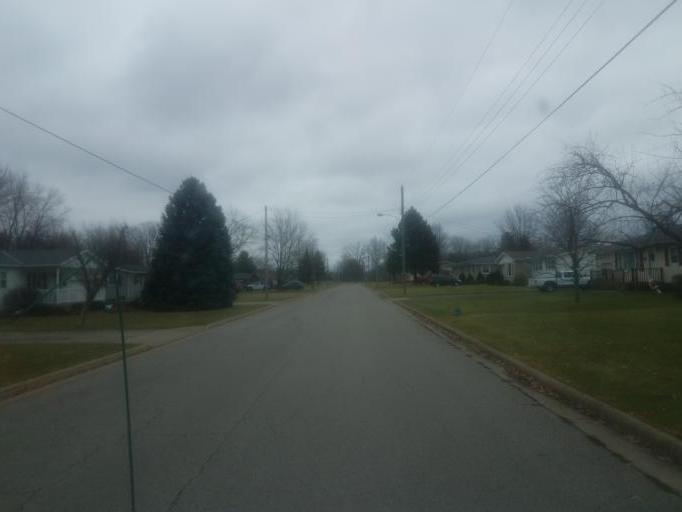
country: US
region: Ohio
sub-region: Crawford County
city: Crestline
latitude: 40.7743
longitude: -82.7353
